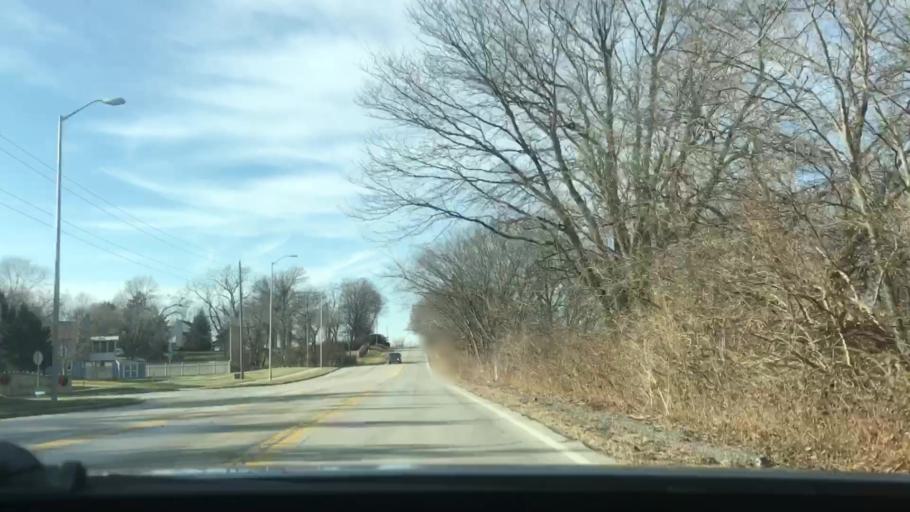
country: US
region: Missouri
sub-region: Clay County
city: Smithville
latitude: 39.3039
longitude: -94.5916
